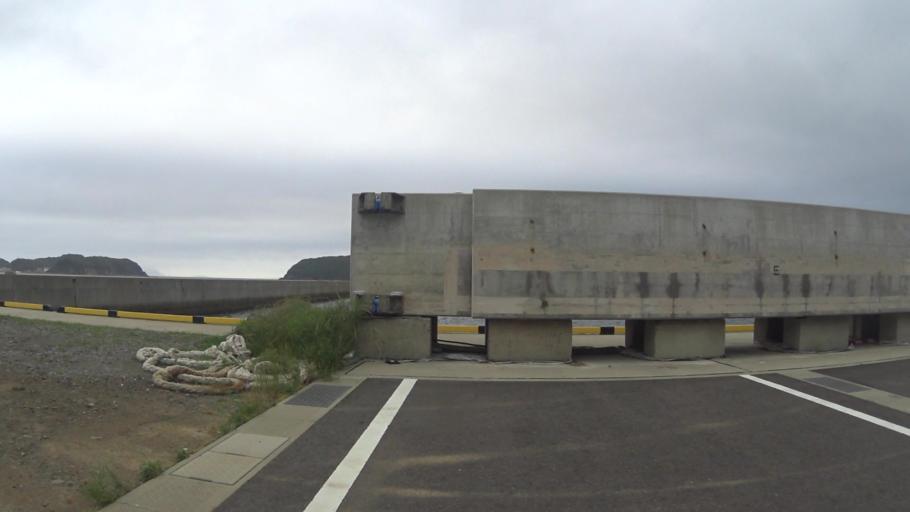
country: JP
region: Nagasaki
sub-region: Hirado Shi
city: Hirado
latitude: 33.1886
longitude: 129.3558
